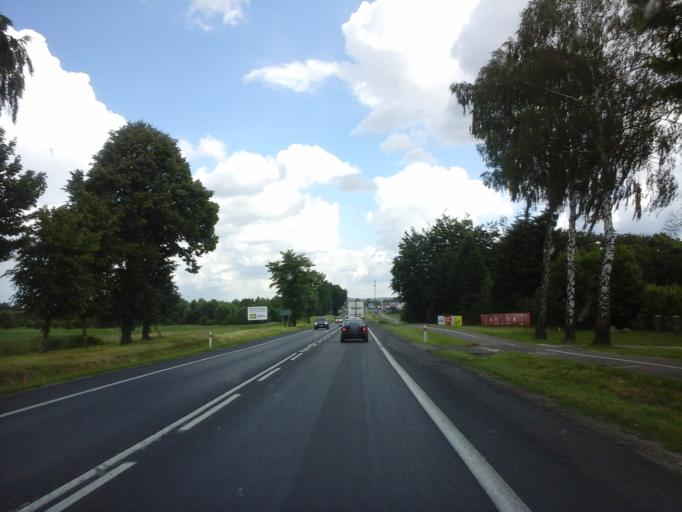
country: PL
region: West Pomeranian Voivodeship
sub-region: Koszalin
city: Koszalin
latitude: 54.1741
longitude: 16.1250
